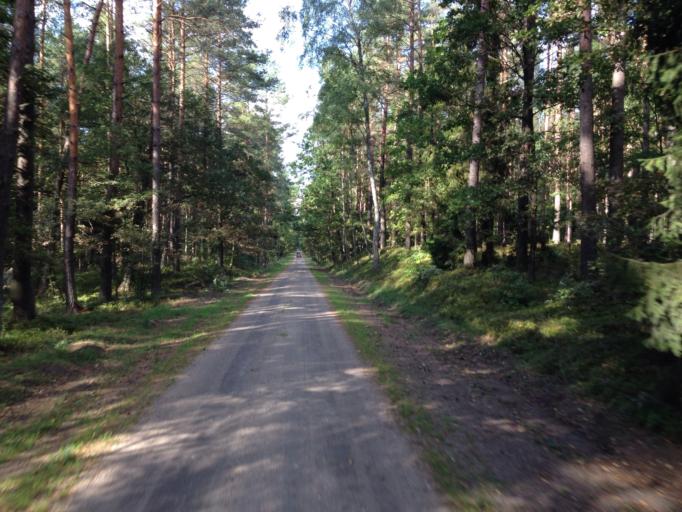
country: PL
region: Kujawsko-Pomorskie
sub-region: Powiat brodnicki
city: Gorzno
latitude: 53.1840
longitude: 19.7004
